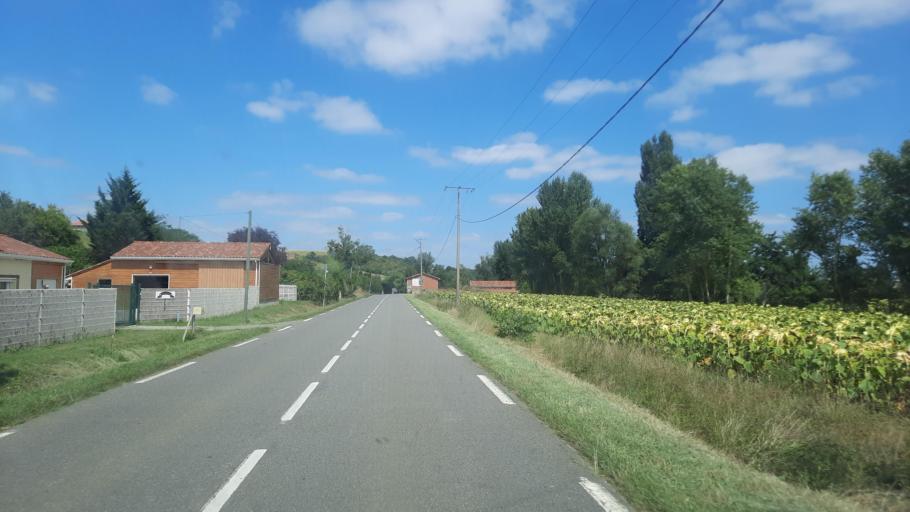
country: FR
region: Midi-Pyrenees
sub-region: Departement du Gers
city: Lombez
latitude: 43.4422
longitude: 0.8547
